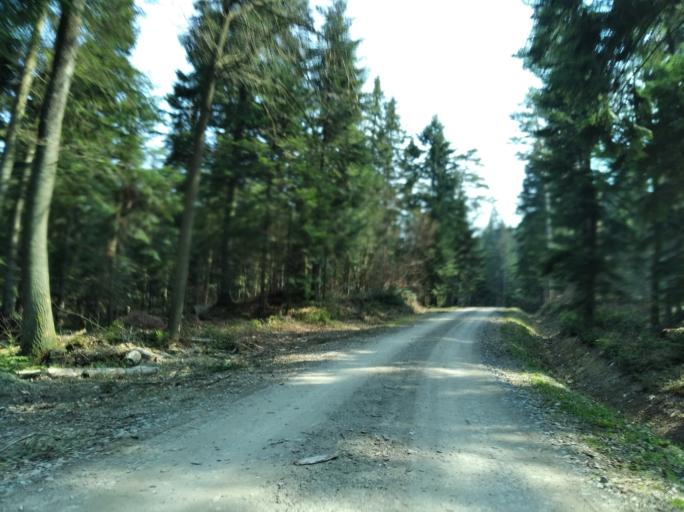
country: PL
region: Subcarpathian Voivodeship
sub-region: Powiat strzyzowski
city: Strzyzow
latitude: 49.8276
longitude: 21.7858
